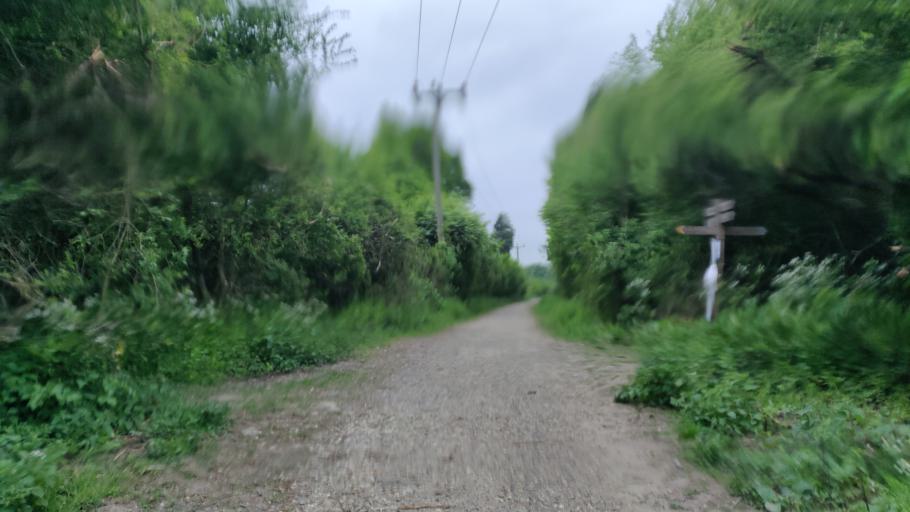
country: GB
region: England
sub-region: West Sussex
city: Partridge Green
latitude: 50.9949
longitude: -0.3159
